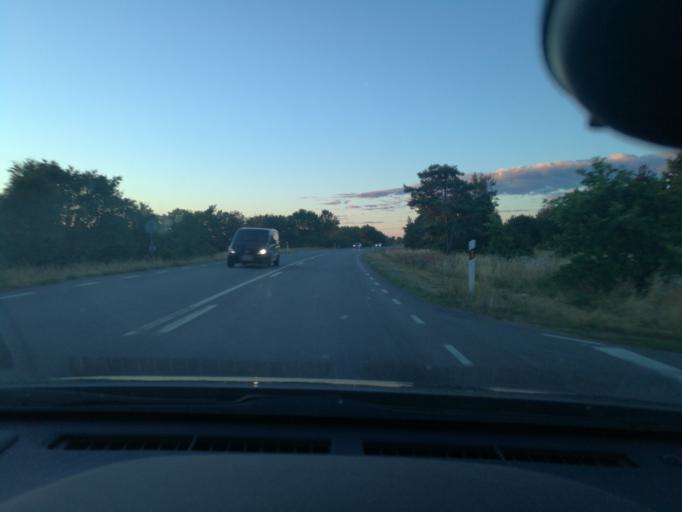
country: SE
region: Kalmar
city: Faerjestaden
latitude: 56.7019
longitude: 16.5234
